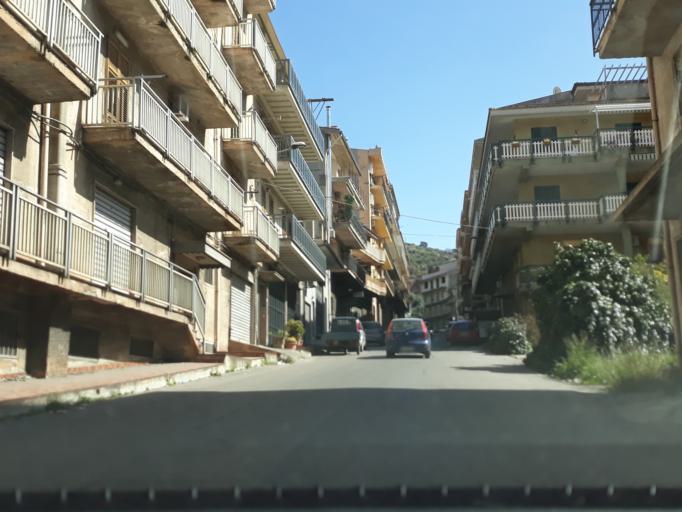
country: IT
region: Sicily
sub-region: Palermo
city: Belmonte Mezzagno
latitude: 38.0468
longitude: 13.3948
